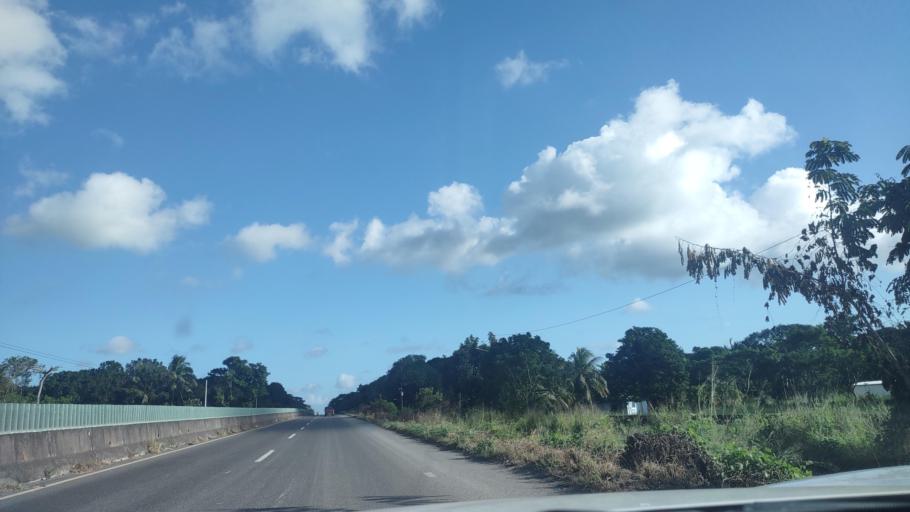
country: MX
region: Veracruz
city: El Tejar
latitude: 19.0641
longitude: -96.1761
